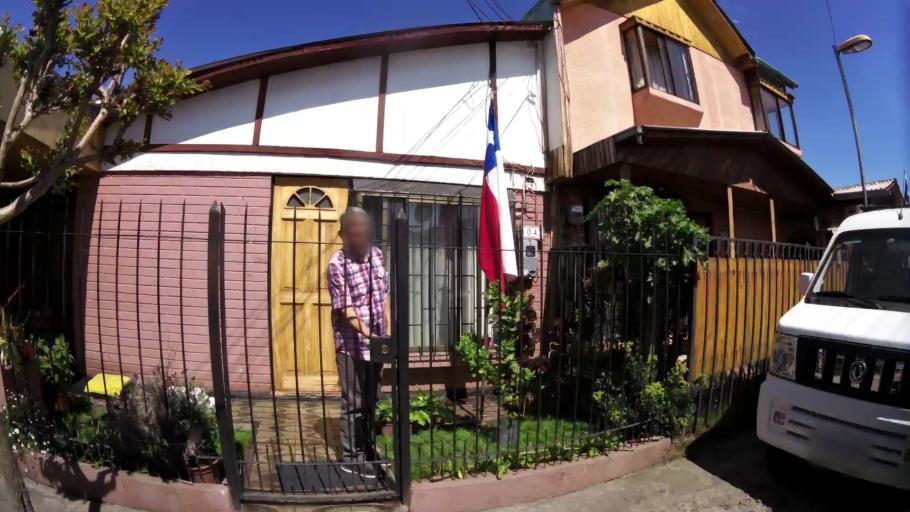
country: CL
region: Santiago Metropolitan
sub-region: Provincia de Santiago
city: Lo Prado
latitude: -33.4957
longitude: -70.7446
